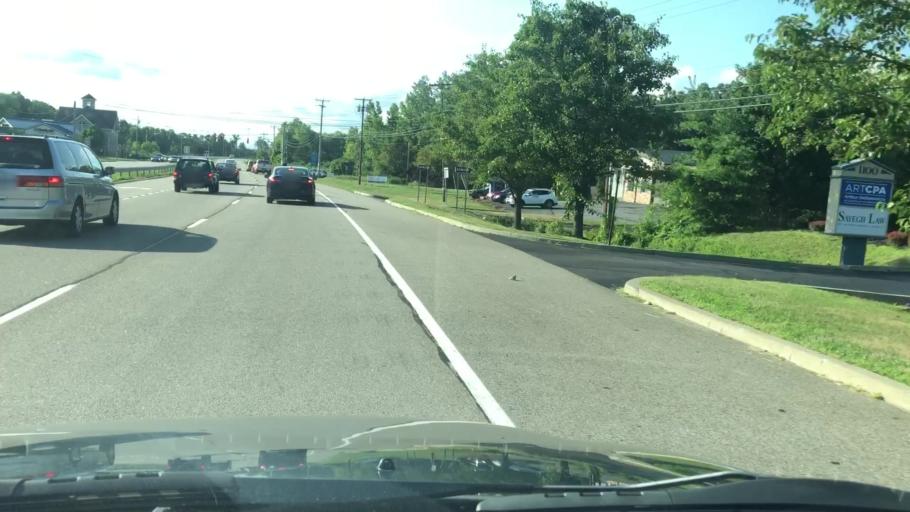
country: US
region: New York
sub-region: Dutchess County
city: Fishkill
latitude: 41.5633
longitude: -73.9043
